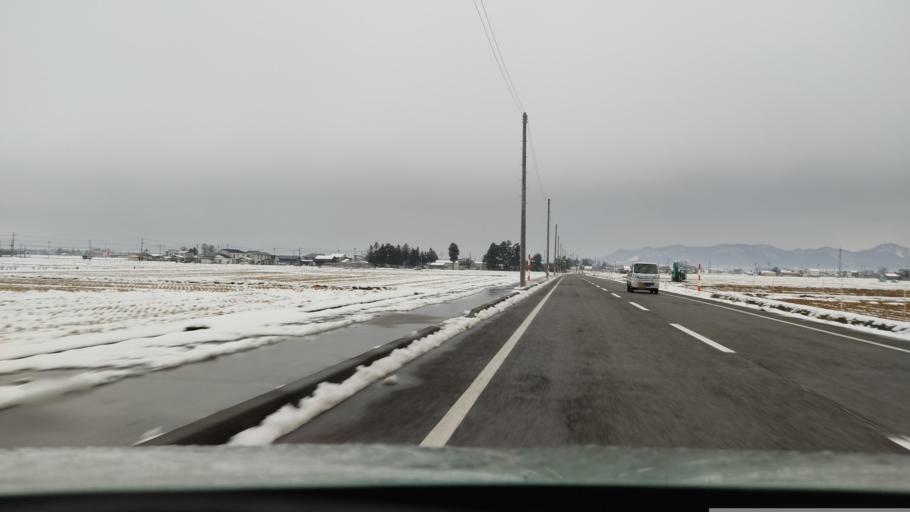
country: JP
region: Akita
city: Omagari
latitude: 39.4294
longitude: 140.5320
